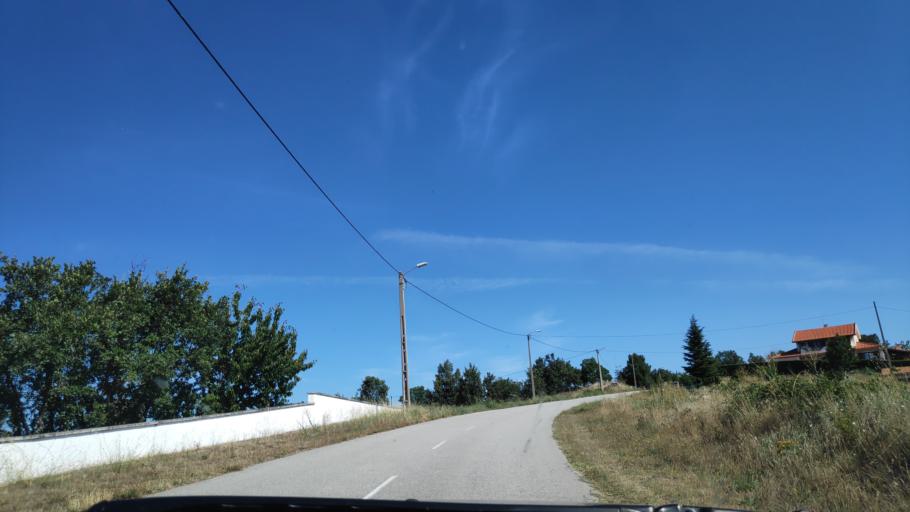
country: ES
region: Castille and Leon
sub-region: Provincia de Zamora
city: Alcanices
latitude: 41.6387
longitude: -6.3551
